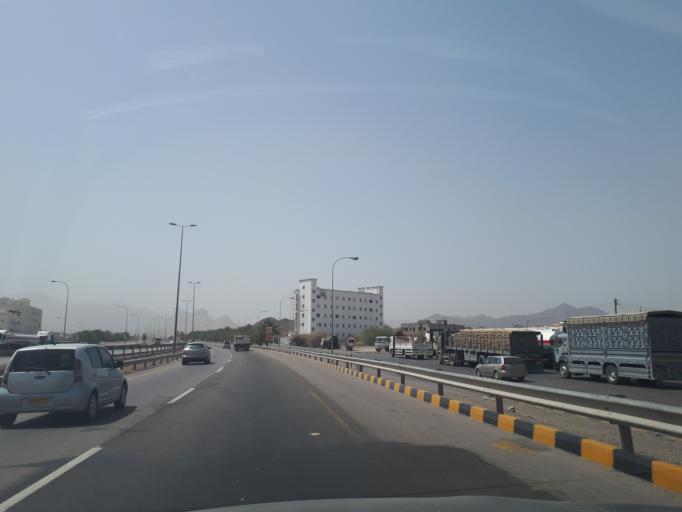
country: OM
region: Muhafazat ad Dakhiliyah
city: Bidbid
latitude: 23.5268
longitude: 58.1887
